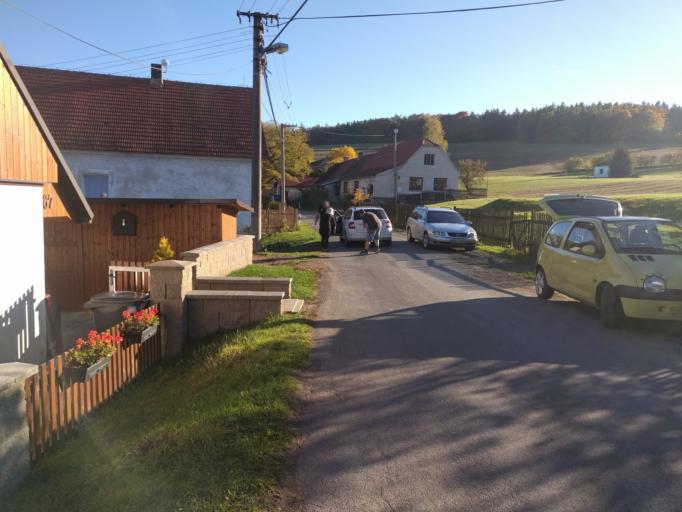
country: CZ
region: Plzensky
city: Zbiroh
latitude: 49.9086
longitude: 13.7263
